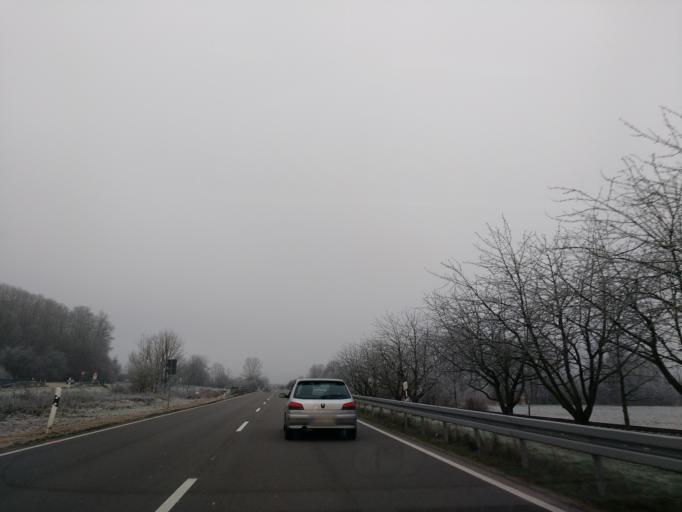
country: DE
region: Baden-Wuerttemberg
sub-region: Freiburg Region
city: Haslach
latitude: 48.5364
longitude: 8.0480
